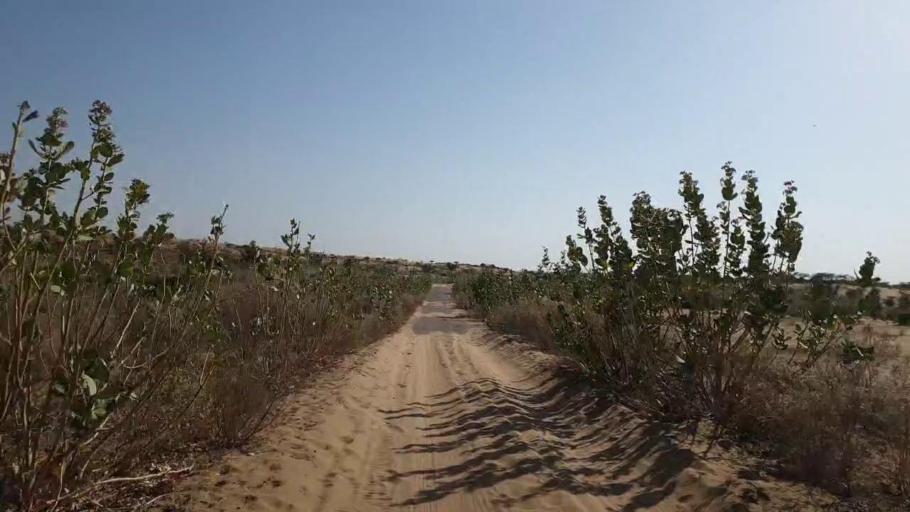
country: PK
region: Sindh
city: Nabisar
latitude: 25.0505
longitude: 70.0216
